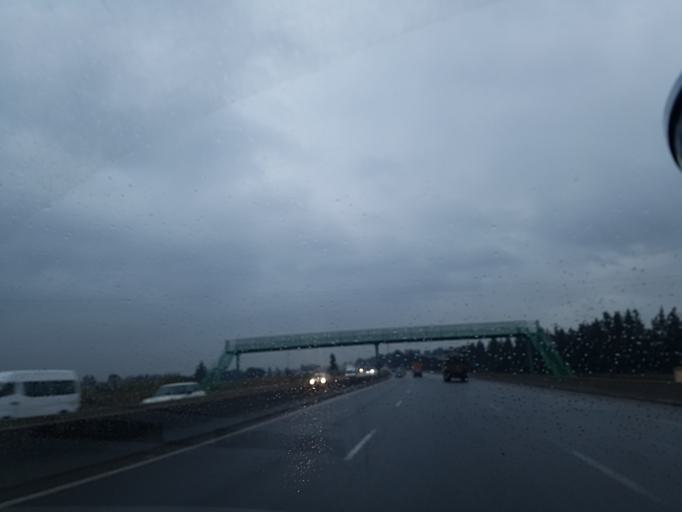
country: DZ
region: Blida
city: Meftah
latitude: 36.6612
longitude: 3.2681
